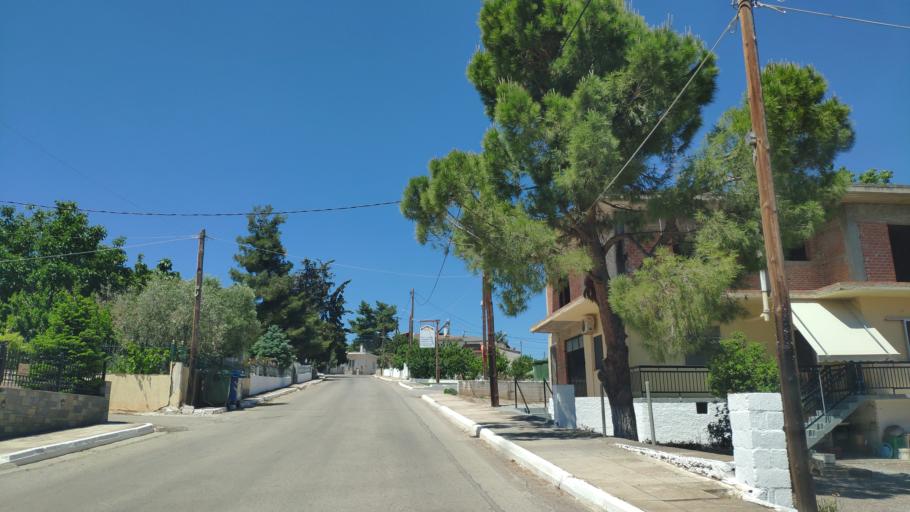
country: GR
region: Central Greece
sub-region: Nomos Voiotias
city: Kaparellion
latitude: 38.2663
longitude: 23.2380
